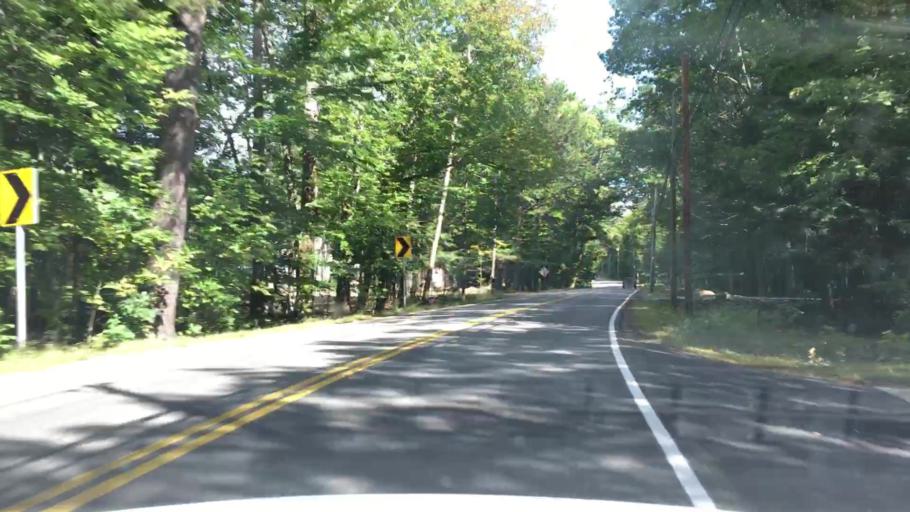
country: US
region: Maine
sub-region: Cumberland County
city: West Scarborough
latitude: 43.6064
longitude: -70.4160
